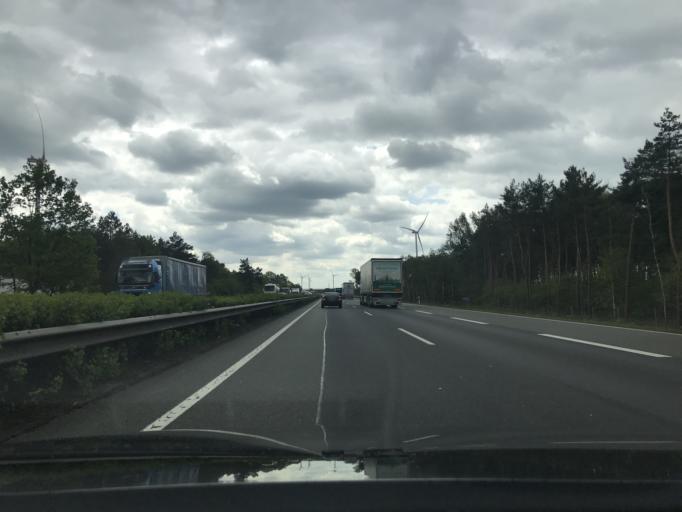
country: DE
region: Lower Saxony
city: Rieste
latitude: 52.4682
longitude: 8.0523
